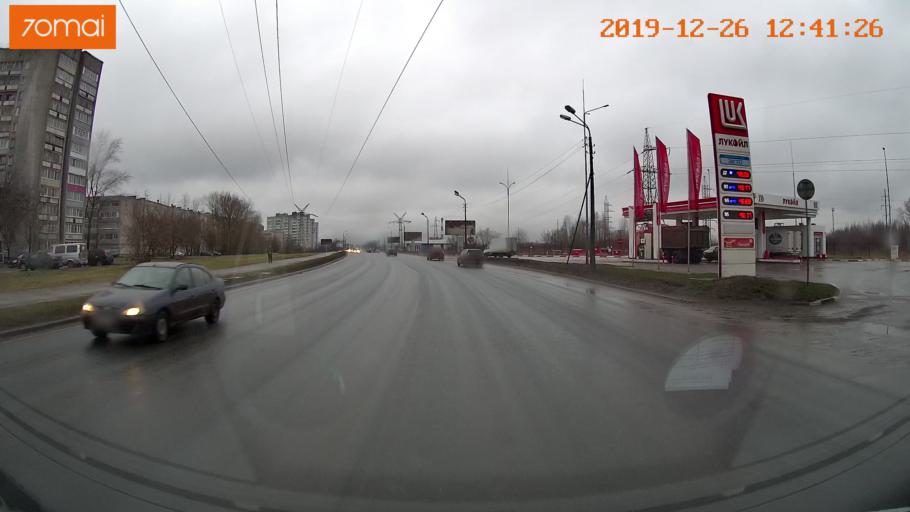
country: RU
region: Vologda
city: Tonshalovo
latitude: 59.1492
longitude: 37.9613
